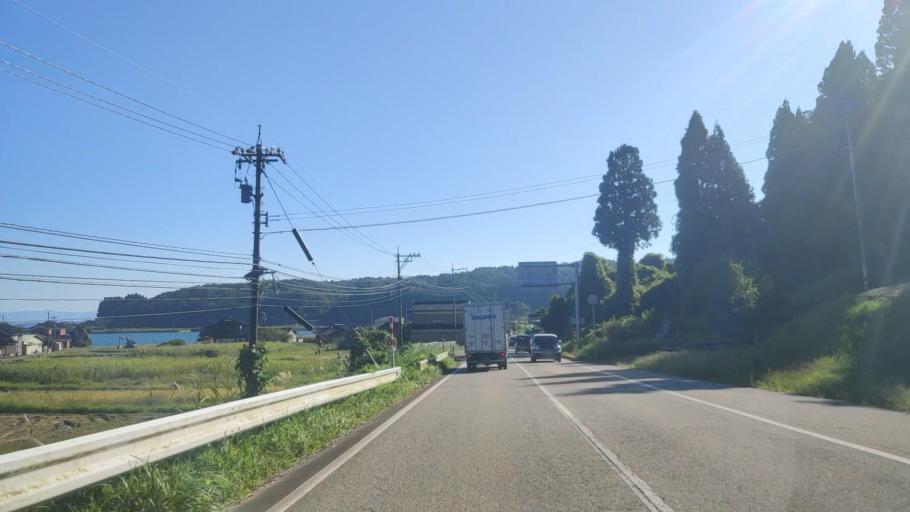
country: JP
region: Ishikawa
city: Nanao
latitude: 37.2061
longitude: 136.9080
